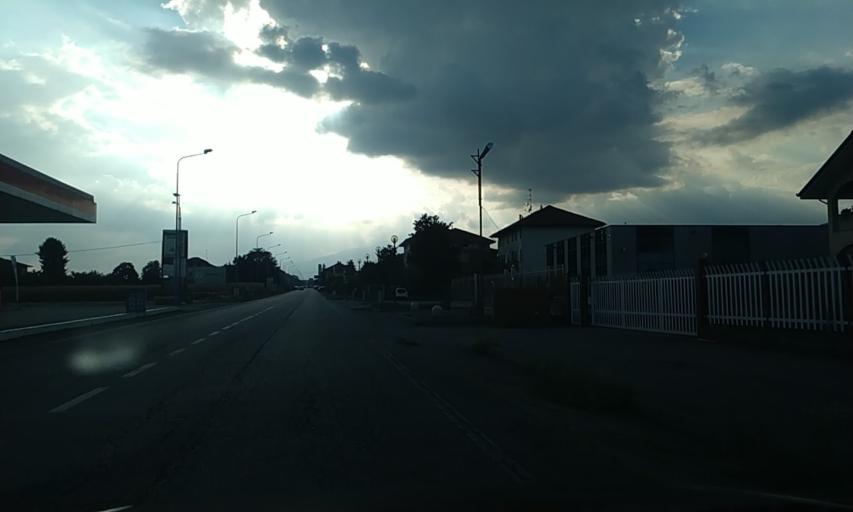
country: IT
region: Piedmont
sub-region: Provincia di Biella
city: Valdengo
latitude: 45.5636
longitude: 8.1336
